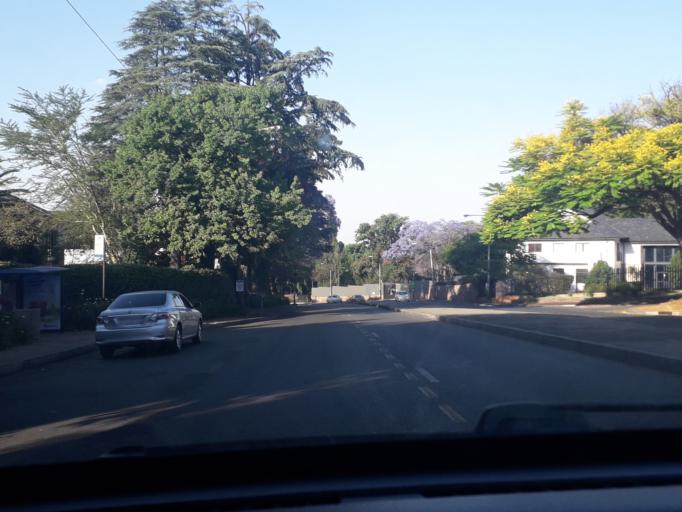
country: ZA
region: Gauteng
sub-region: City of Johannesburg Metropolitan Municipality
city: Johannesburg
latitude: -26.1769
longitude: 28.0308
